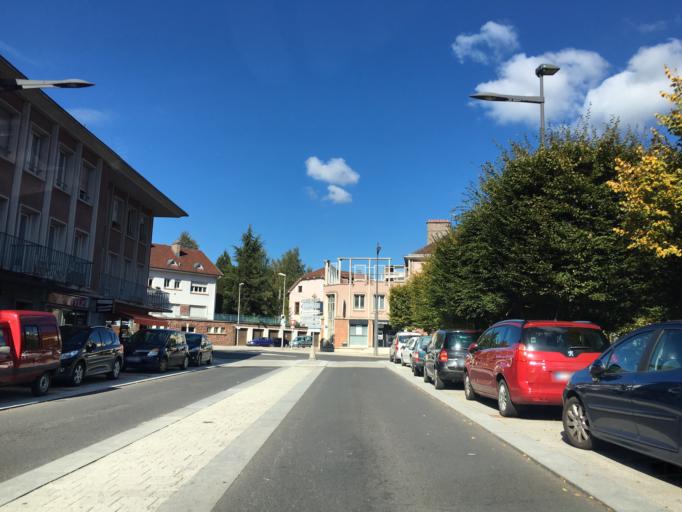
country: FR
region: Lorraine
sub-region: Departement des Vosges
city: Saint-Die-des-Vosges
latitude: 48.2892
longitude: 6.9497
